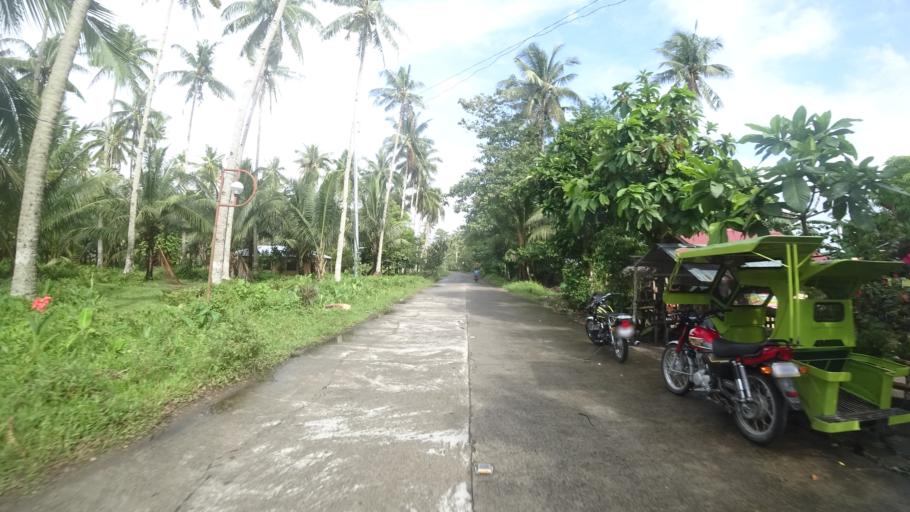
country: PH
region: Eastern Visayas
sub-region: Province of Leyte
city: MacArthur
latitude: 10.8176
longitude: 124.9670
